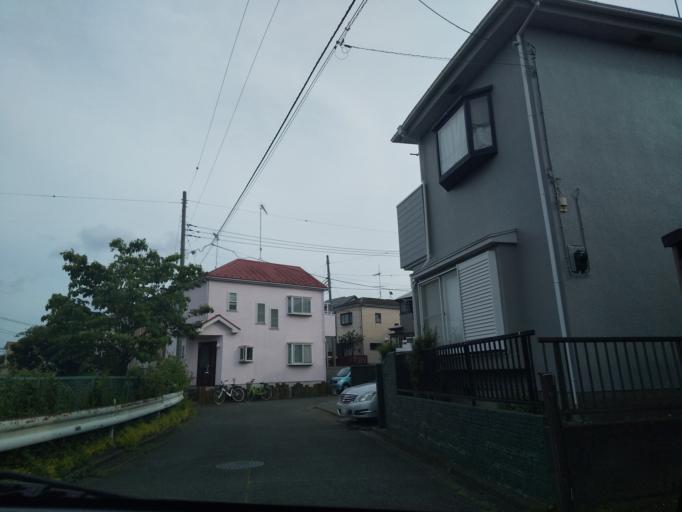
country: JP
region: Kanagawa
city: Zama
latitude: 35.5454
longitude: 139.3698
